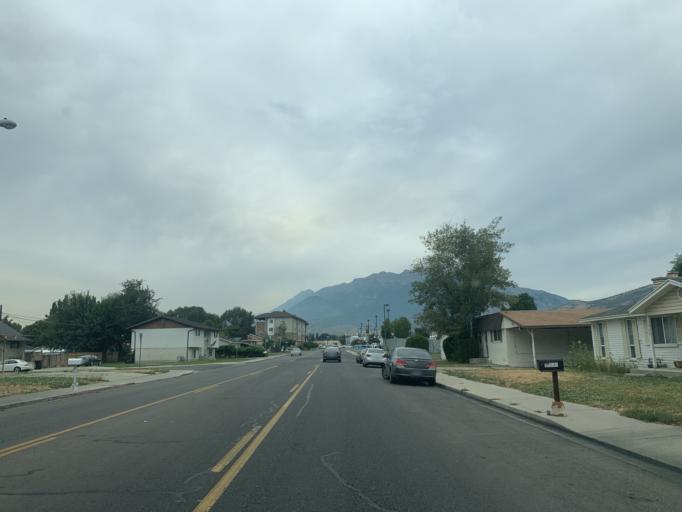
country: US
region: Utah
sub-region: Utah County
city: Provo
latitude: 40.2581
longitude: -111.6680
